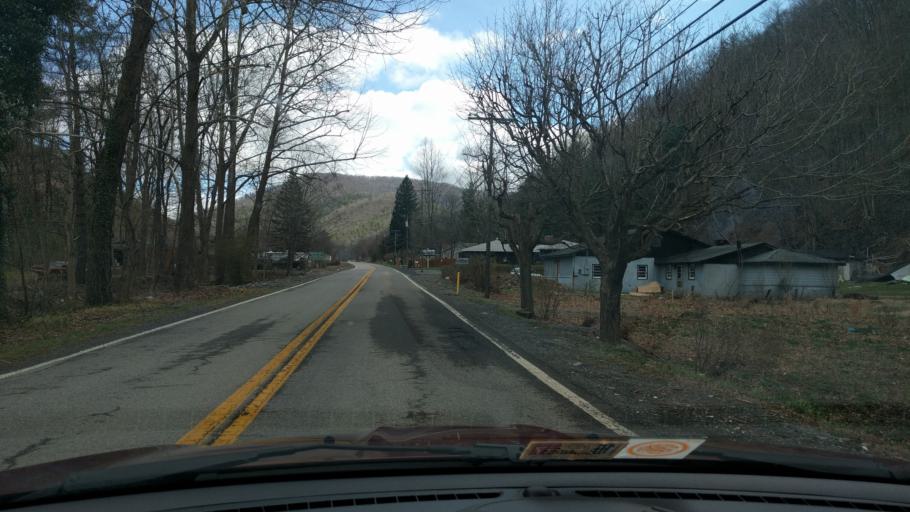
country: US
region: West Virginia
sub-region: Greenbrier County
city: White Sulphur Springs
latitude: 37.7976
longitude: -80.2786
